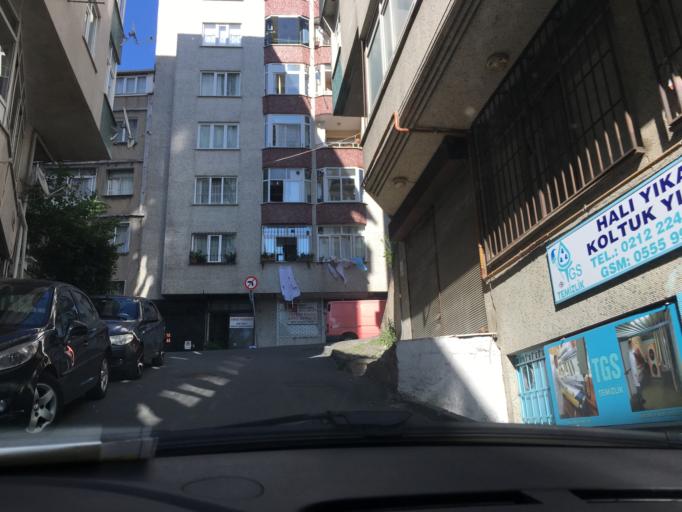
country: TR
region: Istanbul
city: Sisli
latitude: 41.0535
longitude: 28.9745
